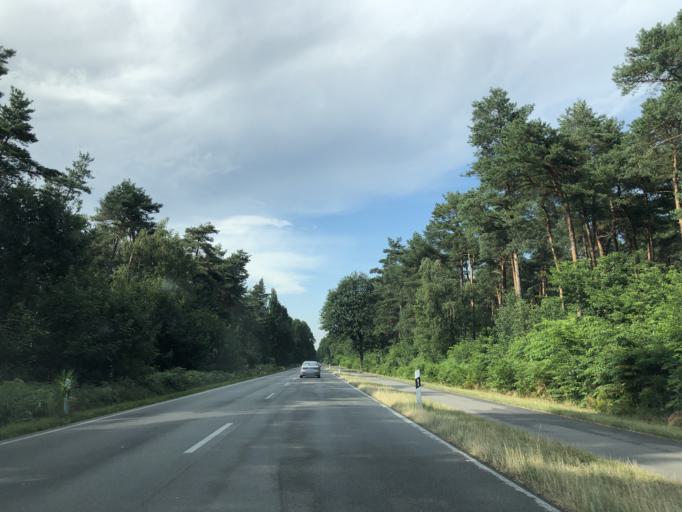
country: DE
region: North Rhine-Westphalia
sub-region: Regierungsbezirk Dusseldorf
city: Kranenburg
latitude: 51.7278
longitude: 6.0367
